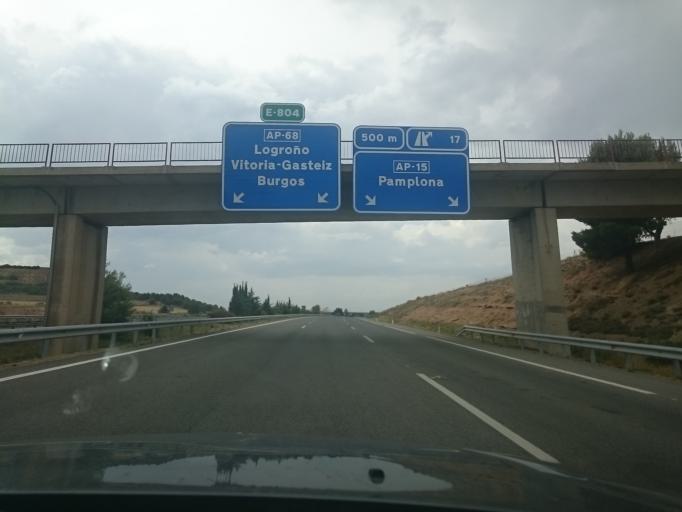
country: ES
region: Navarre
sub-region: Provincia de Navarra
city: Corella
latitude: 42.0859
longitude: -1.7136
